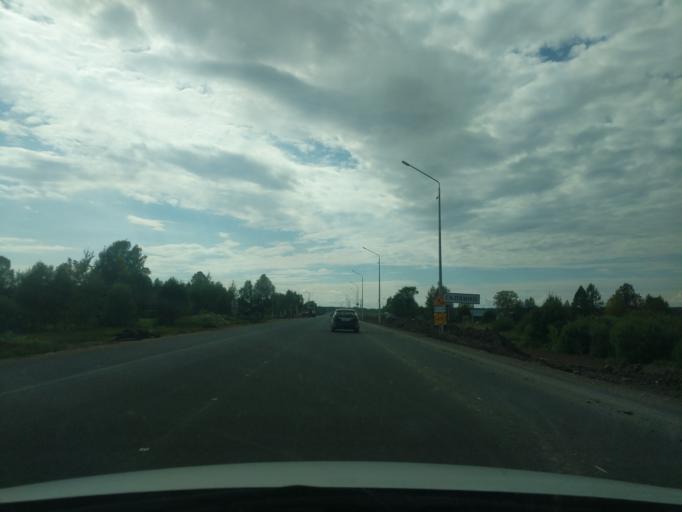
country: RU
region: Kostroma
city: Sudislavl'
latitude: 57.8352
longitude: 41.5545
